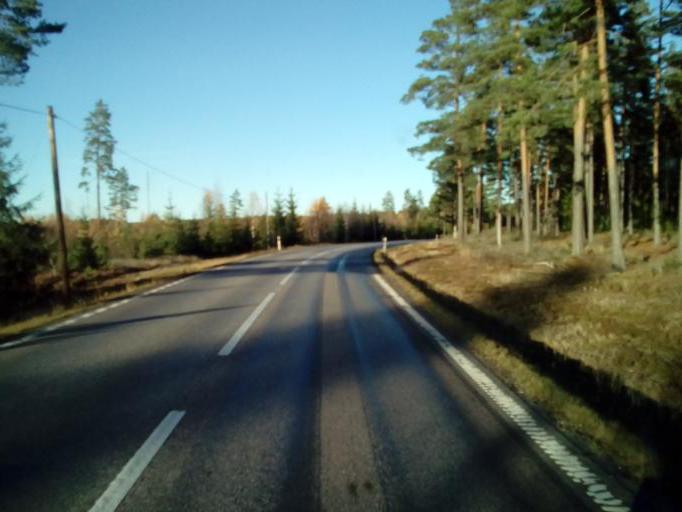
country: SE
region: OErebro
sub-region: Hallsbergs Kommun
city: Palsboda
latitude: 58.8594
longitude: 15.4085
